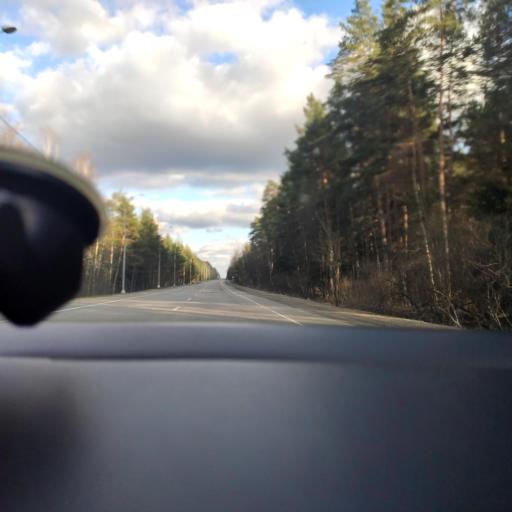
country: RU
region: Moskovskaya
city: Il'inskiy Pogost
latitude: 55.4733
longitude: 38.9564
